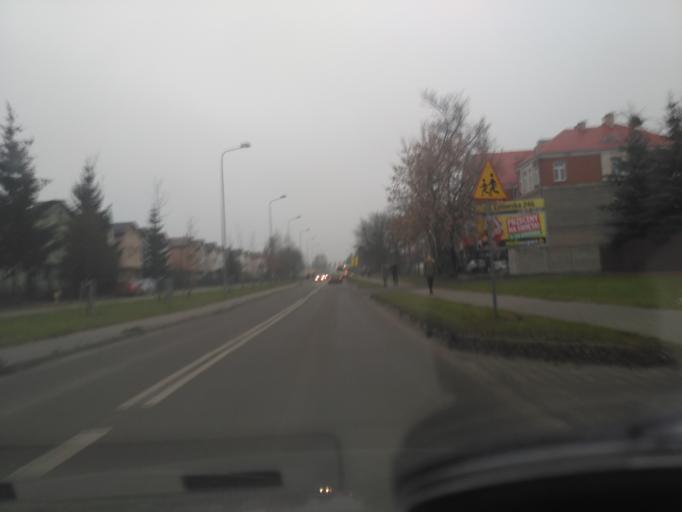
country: PL
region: Lublin Voivodeship
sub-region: Chelm
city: Chelm
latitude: 51.1418
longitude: 23.4553
